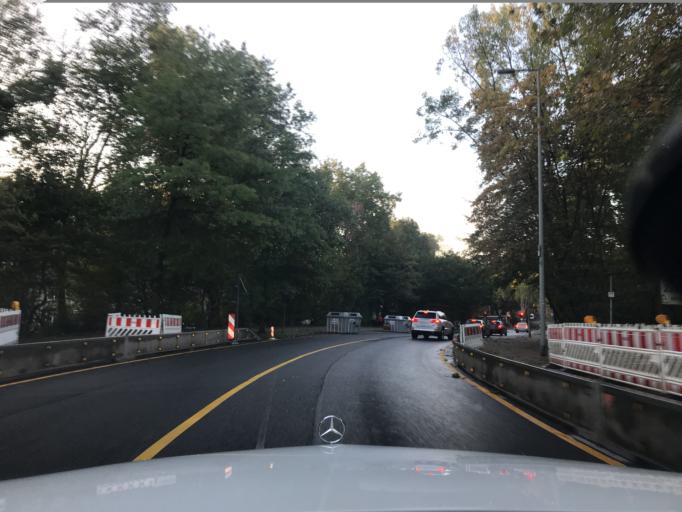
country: DE
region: North Rhine-Westphalia
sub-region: Regierungsbezirk Dusseldorf
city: Oberhausen
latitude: 51.4848
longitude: 6.8273
